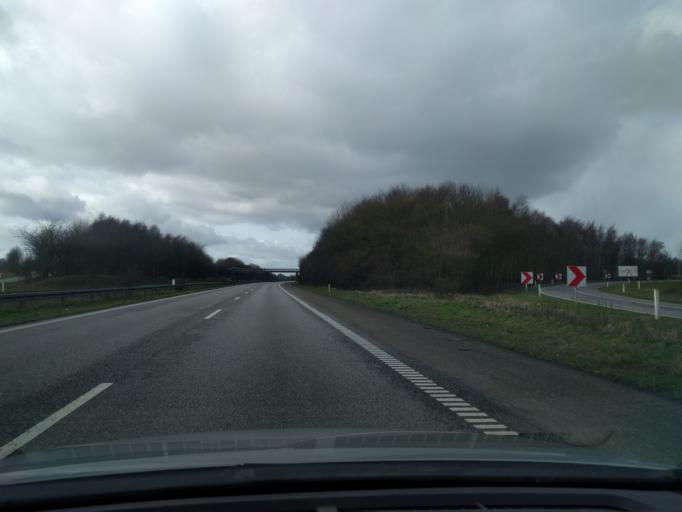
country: DK
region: South Denmark
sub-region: Fredericia Kommune
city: Taulov
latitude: 55.5394
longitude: 9.6427
